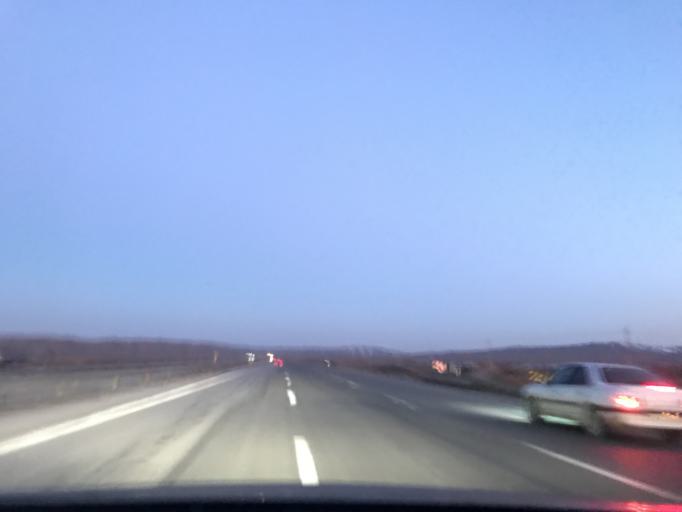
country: IR
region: Isfahan
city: Kashan
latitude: 33.8340
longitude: 51.5976
